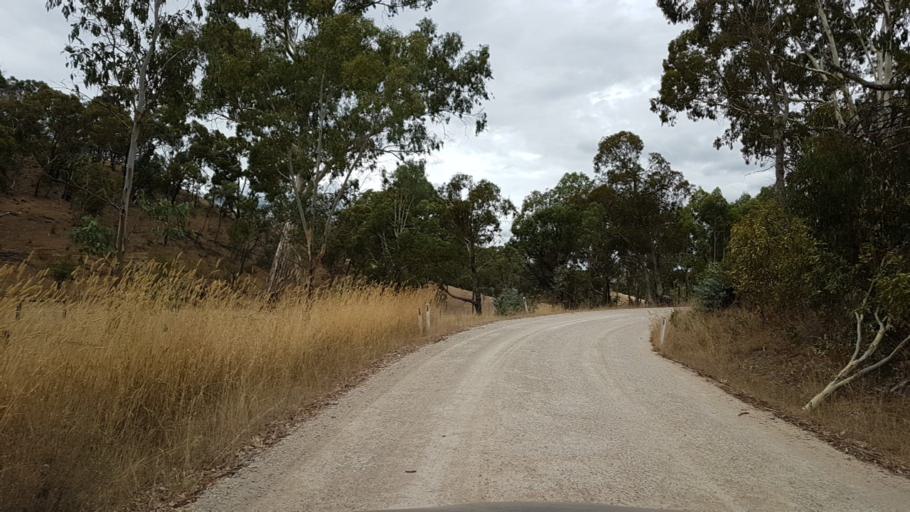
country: AU
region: South Australia
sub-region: Adelaide Hills
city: Gumeracha
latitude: -34.8009
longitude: 138.8269
